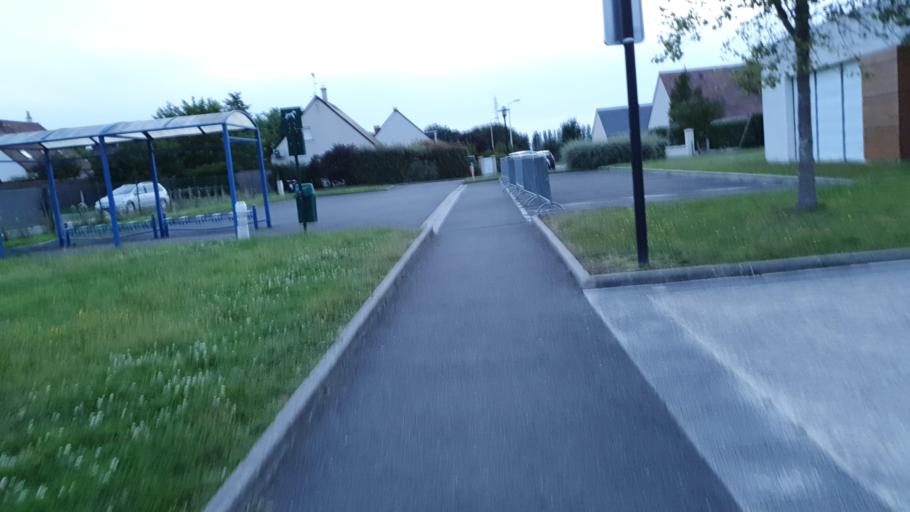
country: FR
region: Centre
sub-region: Departement d'Indre-et-Loire
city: Larcay
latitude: 47.3572
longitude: 0.7696
